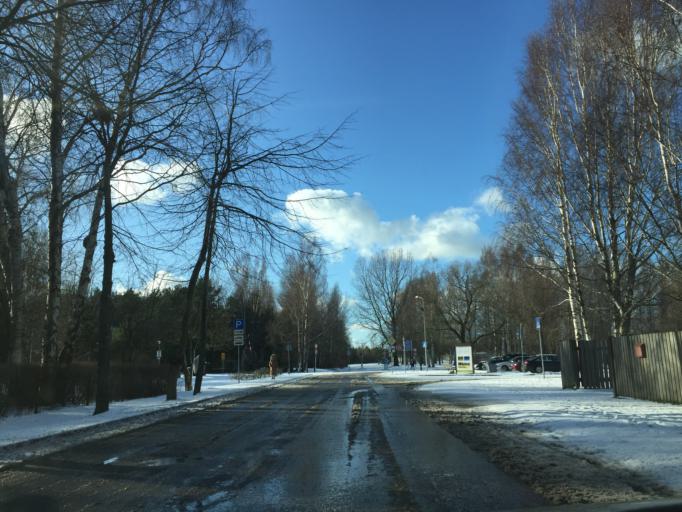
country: LV
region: Ventspils
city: Ventspils
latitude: 57.3889
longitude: 21.5377
